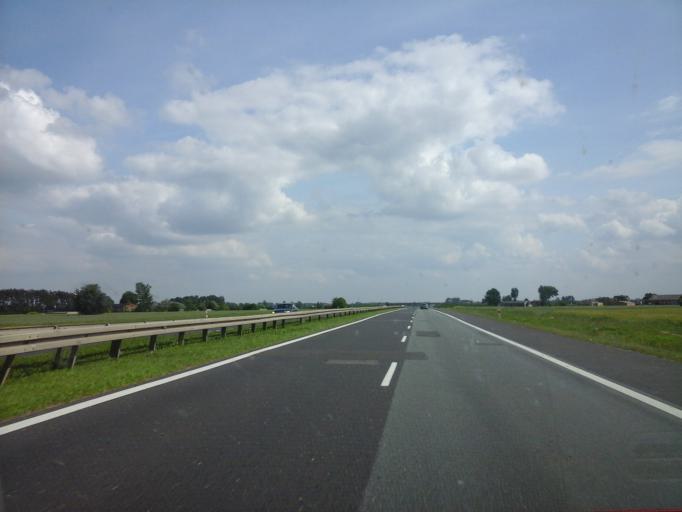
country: PL
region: Lodz Voivodeship
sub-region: Powiat piotrkowski
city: Grabica
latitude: 51.4834
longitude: 19.6205
